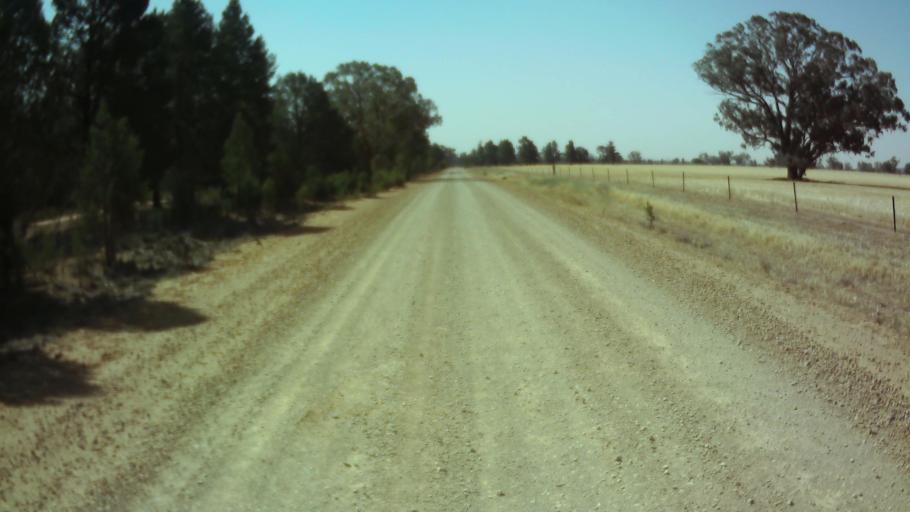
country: AU
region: New South Wales
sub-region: Weddin
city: Grenfell
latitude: -33.9570
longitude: 147.9318
